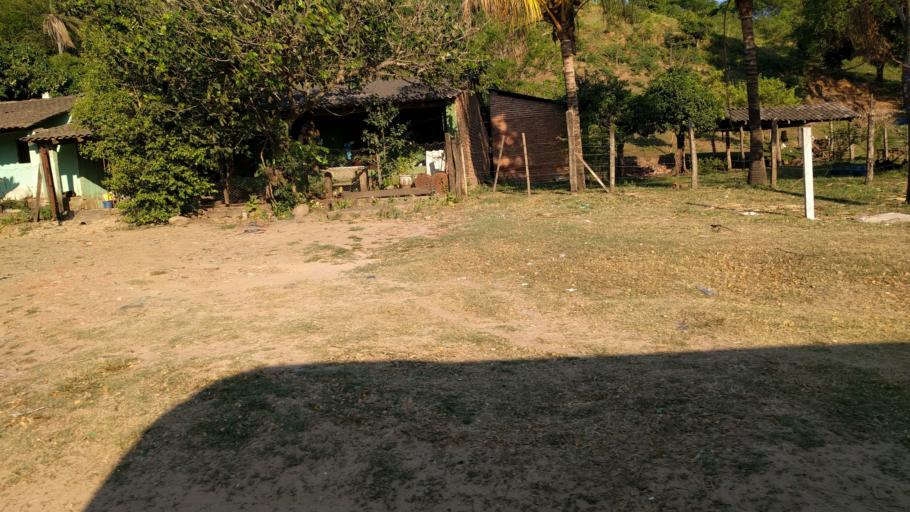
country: BO
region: Santa Cruz
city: Limoncito
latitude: -18.0275
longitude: -63.4019
